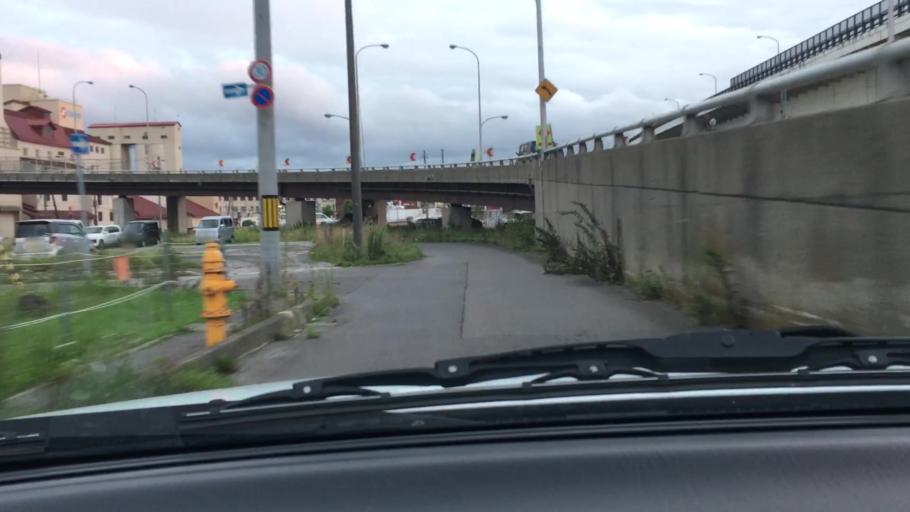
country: JP
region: Hokkaido
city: Hakodate
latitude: 41.7822
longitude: 140.7270
